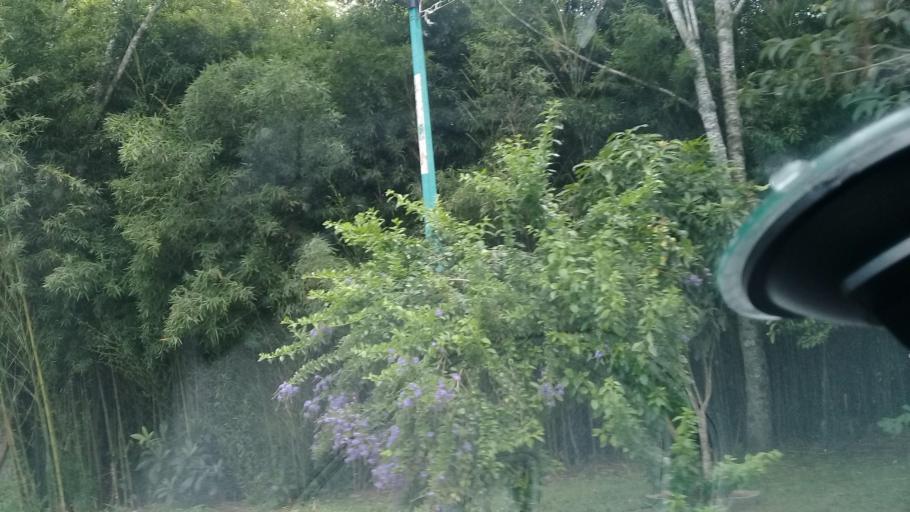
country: MX
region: Veracruz
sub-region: Xalapa
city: Lomas Verdes
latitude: 19.5016
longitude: -96.8892
